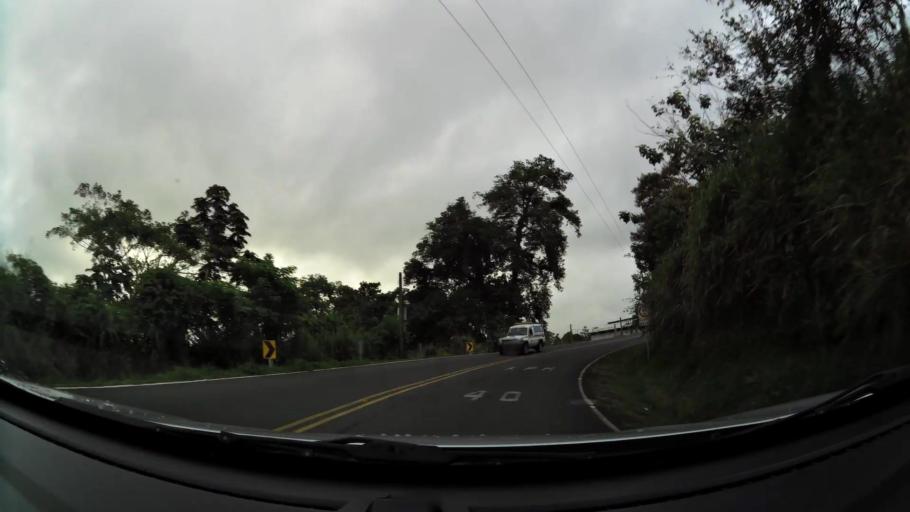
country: CR
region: Cartago
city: Turrialba
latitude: 9.8996
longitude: -83.6890
